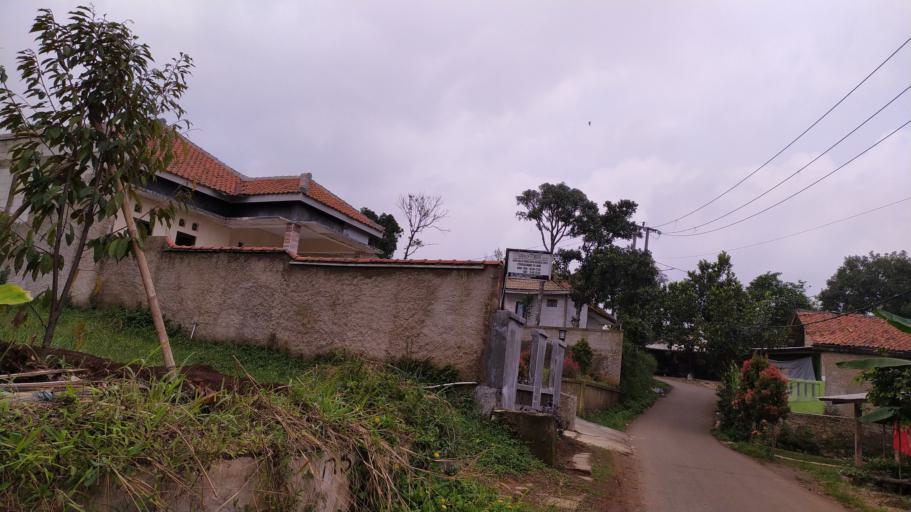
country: ID
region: West Java
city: Ciampea
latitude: -6.6303
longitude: 106.7056
